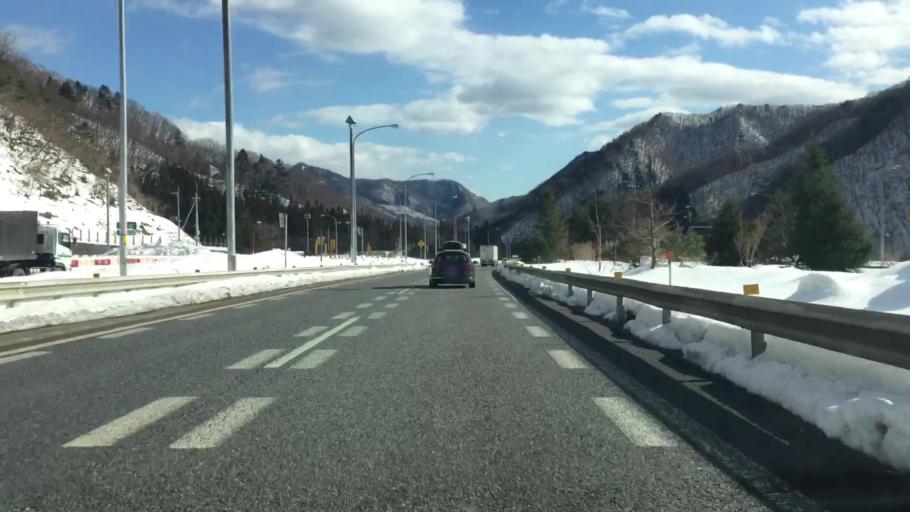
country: JP
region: Gunma
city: Numata
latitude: 36.7789
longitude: 138.9427
